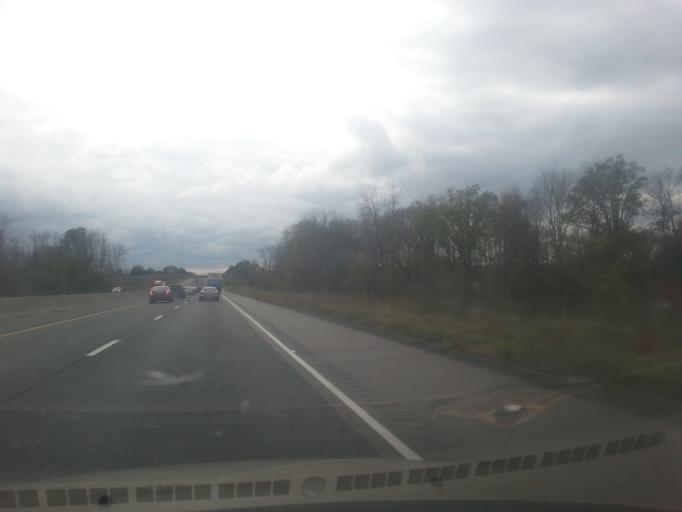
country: CA
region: Ontario
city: Quinte West
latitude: 44.1673
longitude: -77.4976
